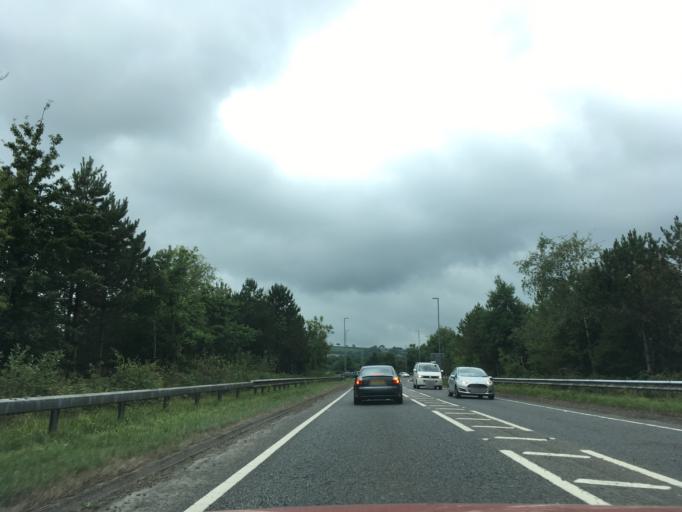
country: GB
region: Wales
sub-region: Carmarthenshire
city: Whitland
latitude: 51.8225
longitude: -4.6241
